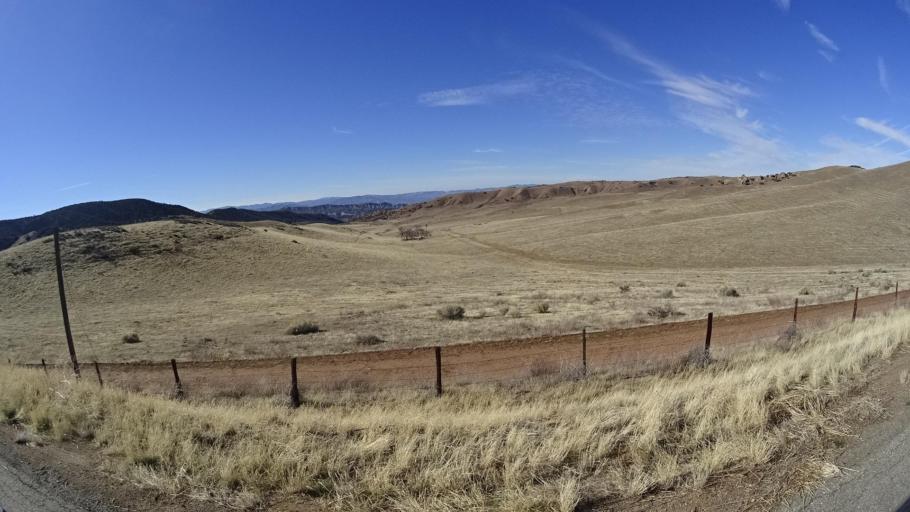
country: US
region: California
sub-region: Kern County
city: Maricopa
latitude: 34.8887
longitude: -119.3561
